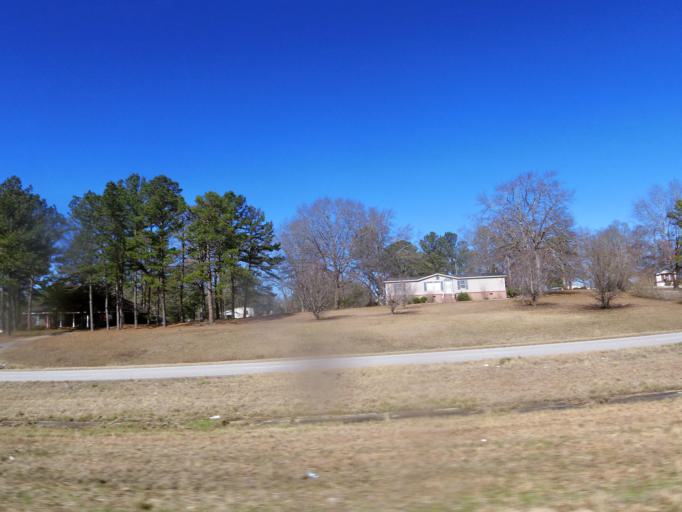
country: US
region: Alabama
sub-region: Bullock County
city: Union Springs
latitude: 32.1461
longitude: -85.6658
